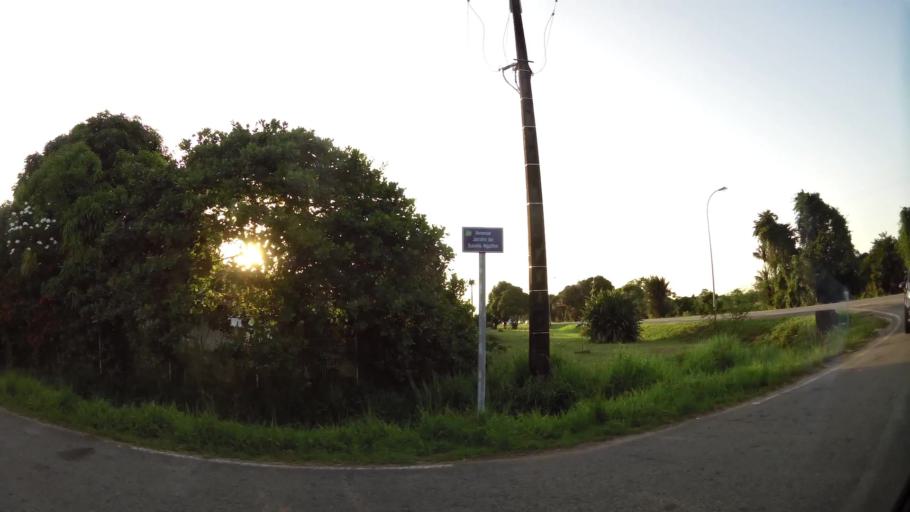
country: GF
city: Macouria
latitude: 5.0090
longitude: -52.4678
